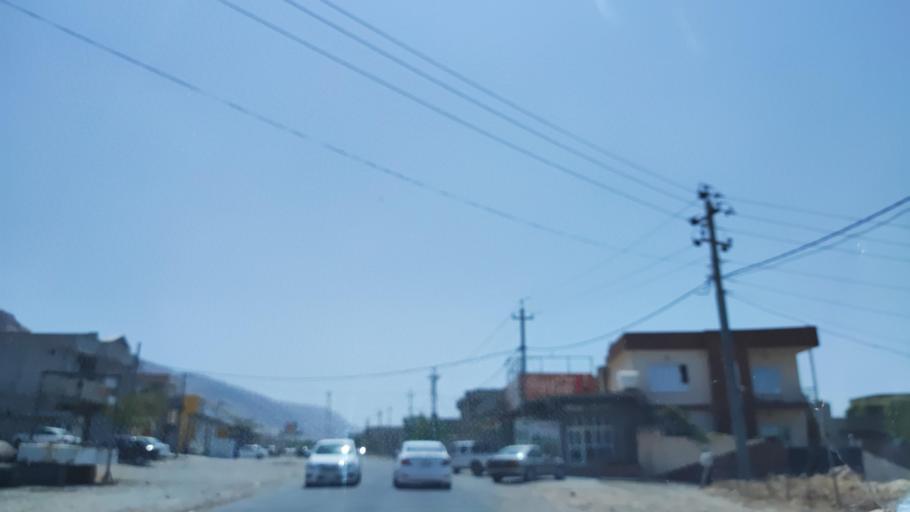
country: IQ
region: Arbil
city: Shaqlawah
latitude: 36.5696
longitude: 44.3343
